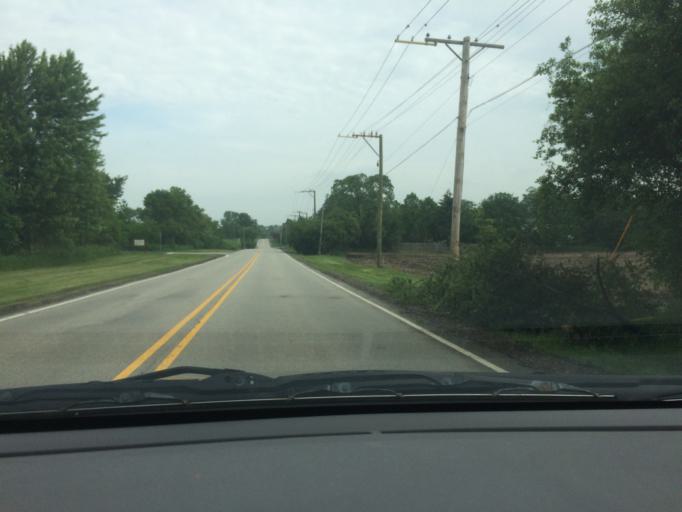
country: US
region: Illinois
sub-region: DuPage County
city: Carol Stream
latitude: 41.9304
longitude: -88.1747
